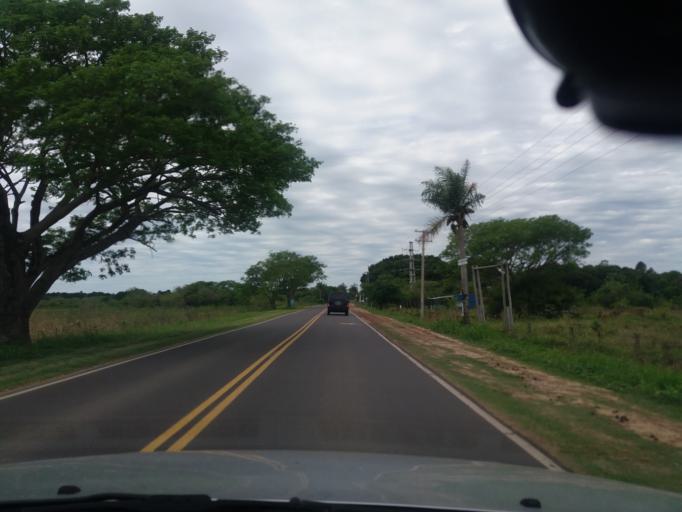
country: AR
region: Corrientes
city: Corrientes
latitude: -27.4497
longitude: -58.7429
